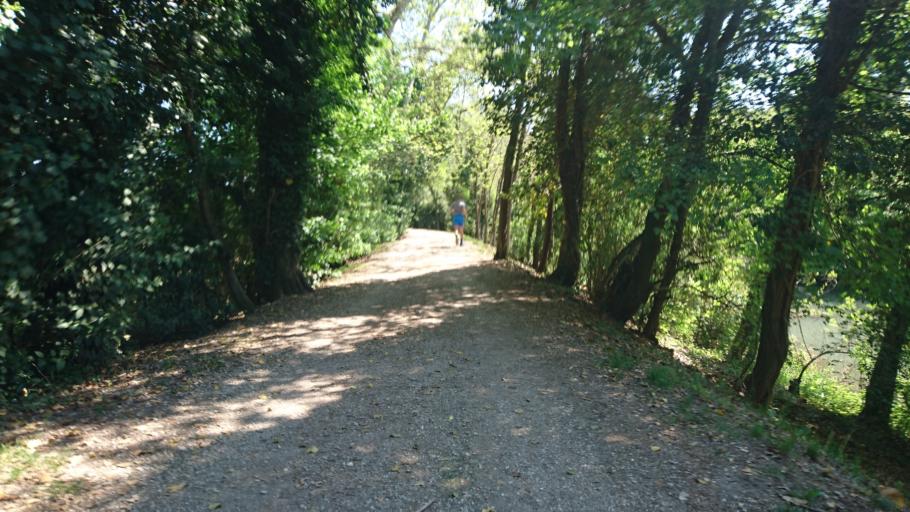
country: IT
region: Veneto
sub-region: Provincia di Treviso
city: Casier
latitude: 45.6441
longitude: 12.2788
